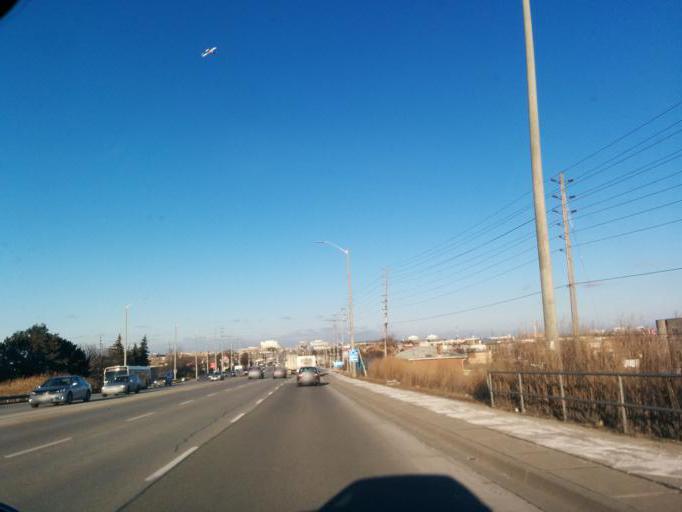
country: CA
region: Ontario
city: Mississauga
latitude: 43.6244
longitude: -79.6331
